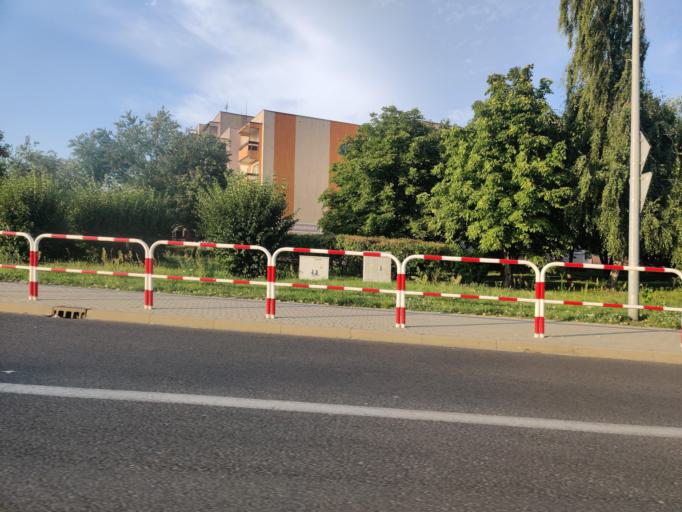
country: PL
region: Greater Poland Voivodeship
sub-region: Konin
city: Konin
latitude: 52.2339
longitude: 18.2472
